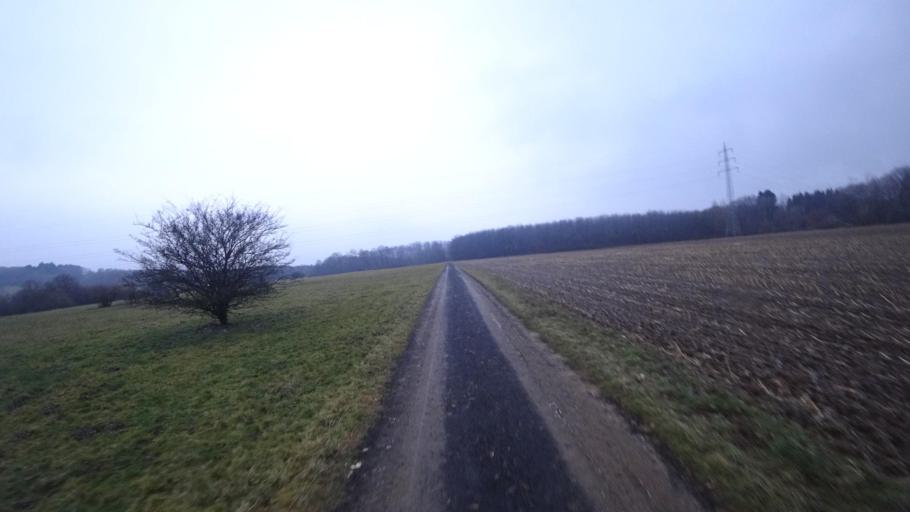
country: DE
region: Rheinland-Pfalz
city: Ailertchen
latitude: 50.6051
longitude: 7.9206
